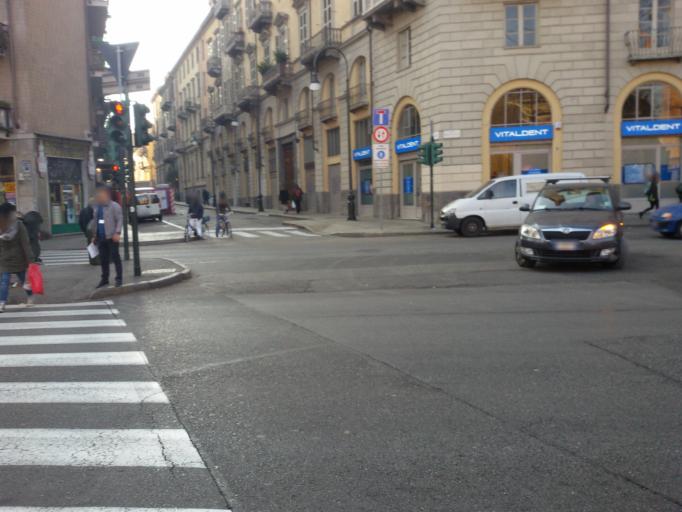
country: IT
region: Piedmont
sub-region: Provincia di Torino
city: Turin
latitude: 45.0705
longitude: 7.6941
